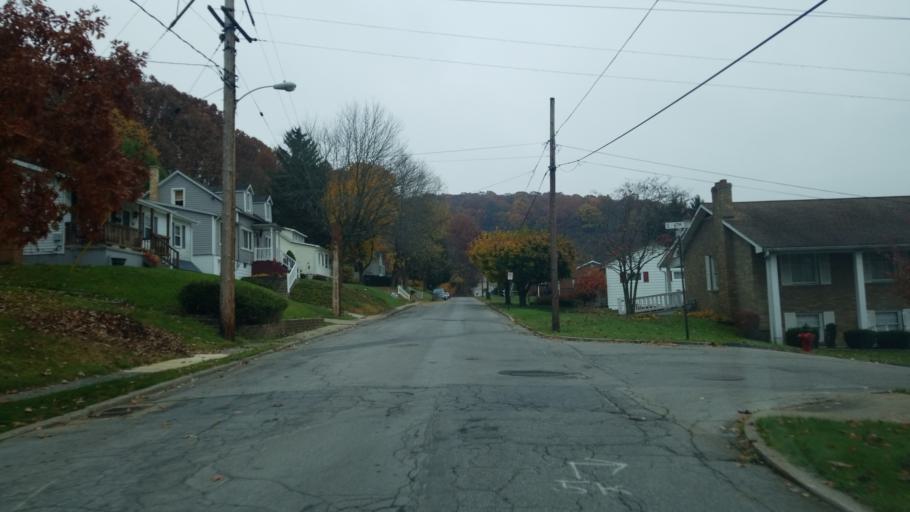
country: US
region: Pennsylvania
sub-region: Clearfield County
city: Clearfield
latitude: 41.0134
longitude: -78.4336
